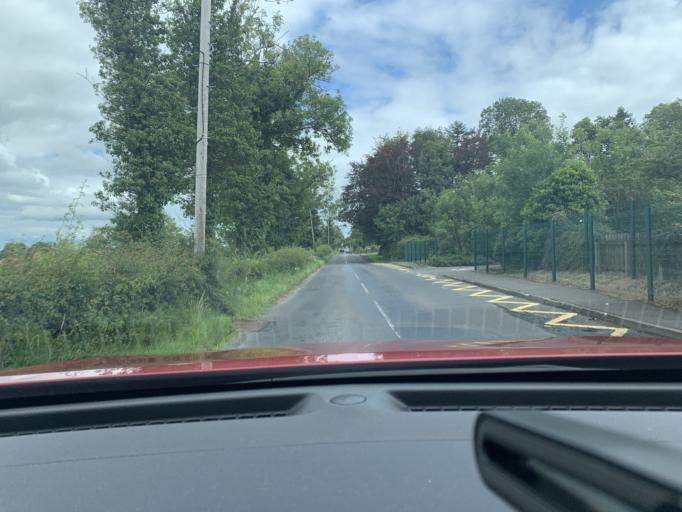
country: GB
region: Northern Ireland
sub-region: Fermanagh District
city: Enniskillen
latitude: 54.2663
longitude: -7.7153
